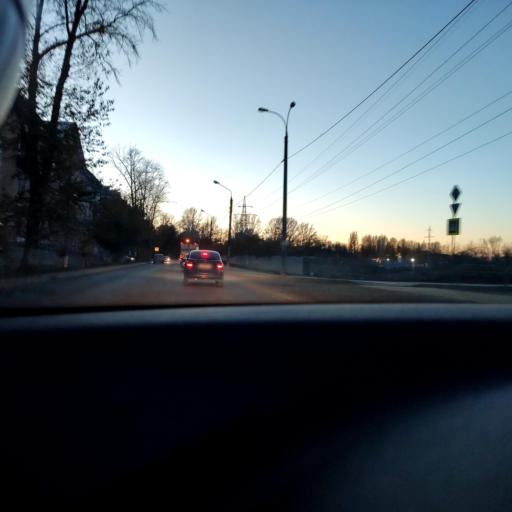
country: RU
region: Samara
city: Petra-Dubrava
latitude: 53.3033
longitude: 50.2850
